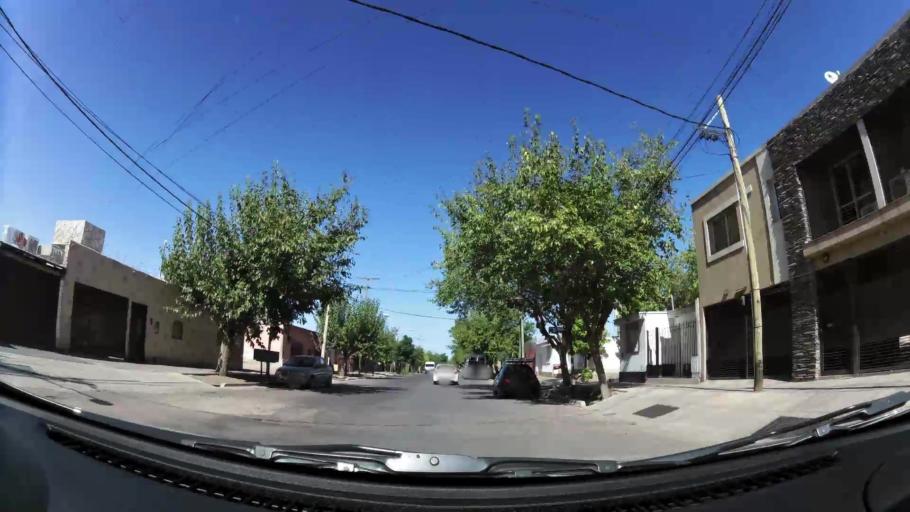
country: AR
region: Mendoza
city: Villa Nueva
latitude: -32.8964
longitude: -68.7942
